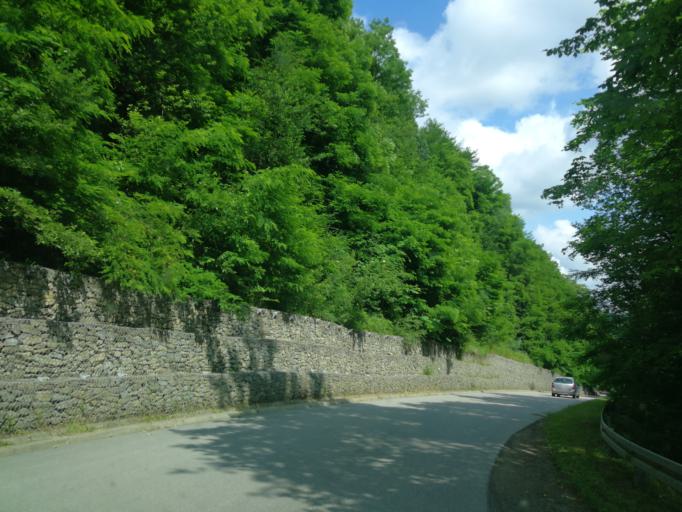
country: PL
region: Subcarpathian Voivodeship
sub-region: Powiat leski
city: Polanczyk
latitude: 49.4177
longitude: 22.4360
